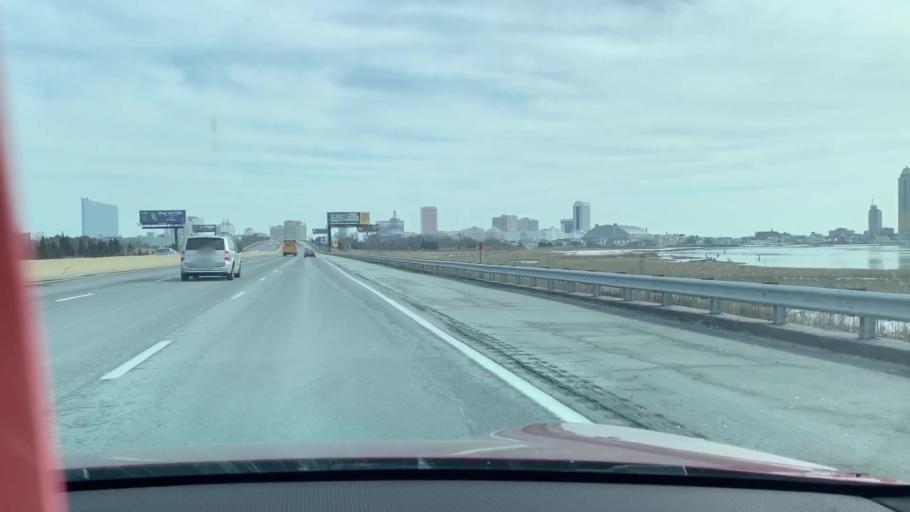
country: US
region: New Jersey
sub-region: Atlantic County
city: Atlantic City
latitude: 39.3661
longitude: -74.4542
